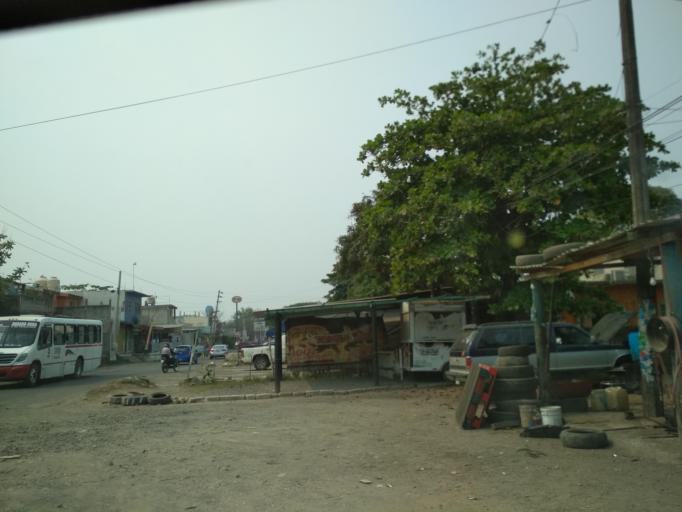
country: MX
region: Veracruz
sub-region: Veracruz
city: Las Amapolas
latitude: 19.1610
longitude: -96.2215
